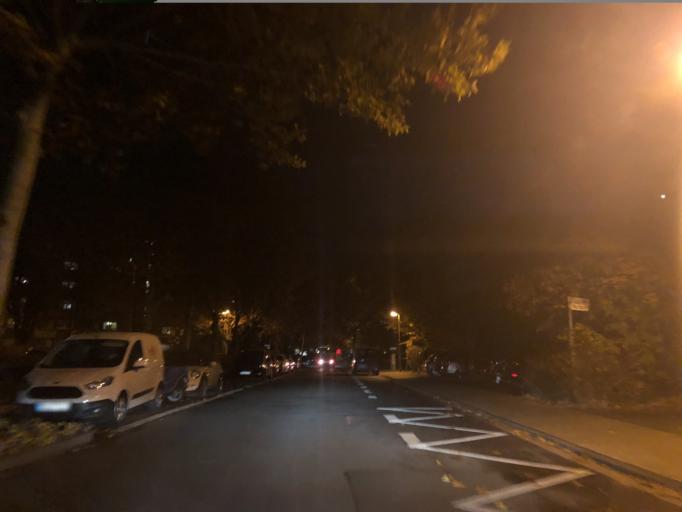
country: DE
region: Hesse
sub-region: Regierungsbezirk Darmstadt
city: Hochheim am Main
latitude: 50.0153
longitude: 8.3427
